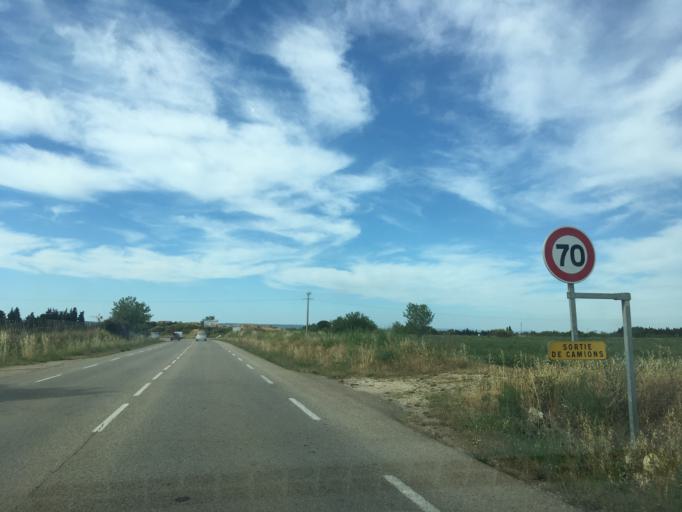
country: FR
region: Languedoc-Roussillon
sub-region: Departement du Gard
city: Garons
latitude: 43.7803
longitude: 4.4300
